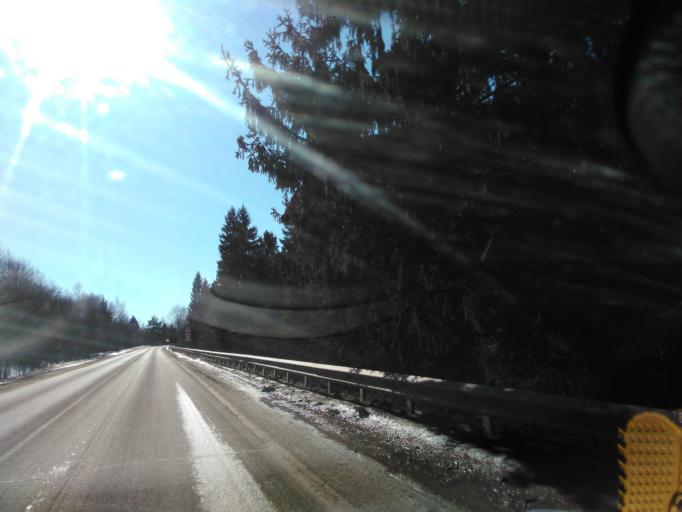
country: RU
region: Moskovskaya
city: Dedenevo
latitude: 56.2643
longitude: 37.5681
